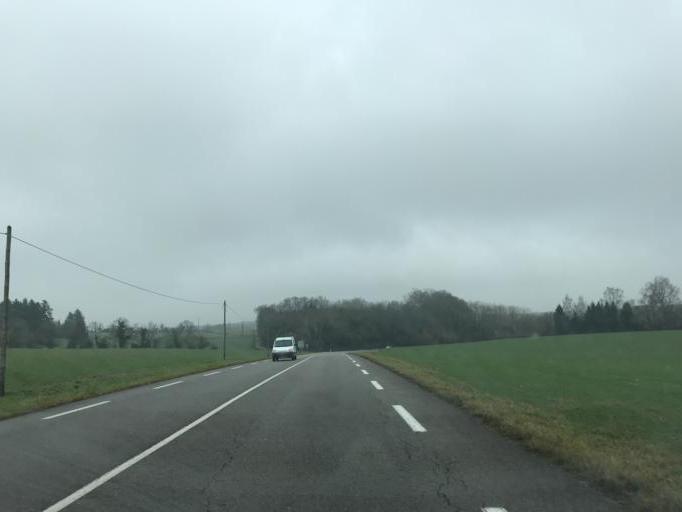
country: FR
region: Rhone-Alpes
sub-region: Departement de l'Ain
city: Peronnas
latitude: 46.1631
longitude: 5.1906
